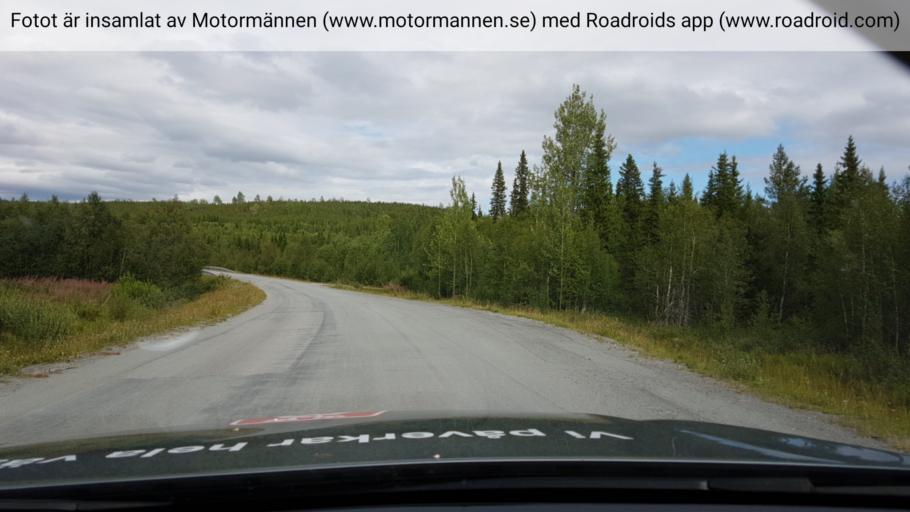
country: SE
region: Jaemtland
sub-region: Krokoms Kommun
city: Valla
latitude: 63.6836
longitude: 13.6820
